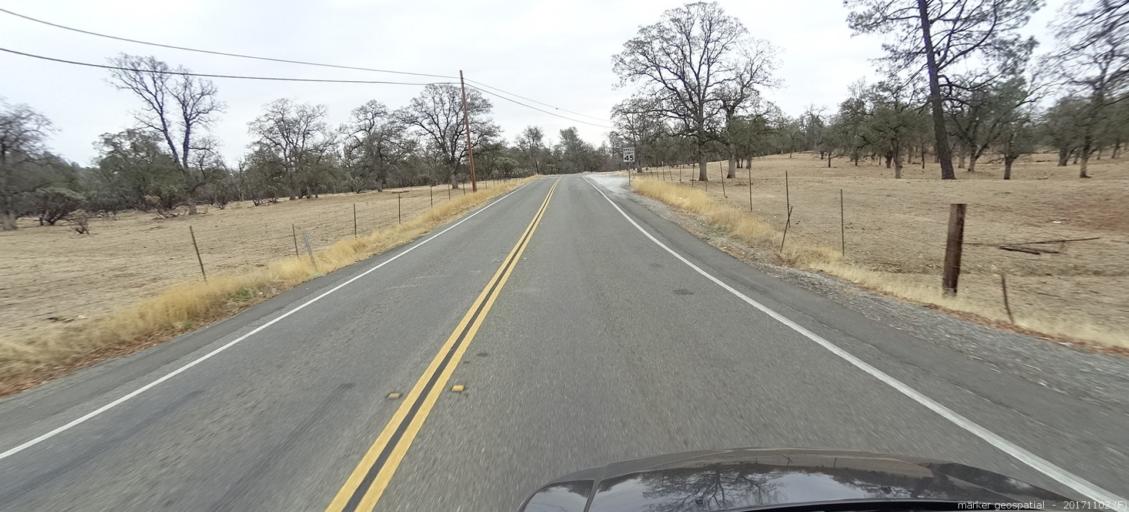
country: US
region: California
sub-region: Shasta County
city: Shasta Lake
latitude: 40.6727
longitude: -122.3219
